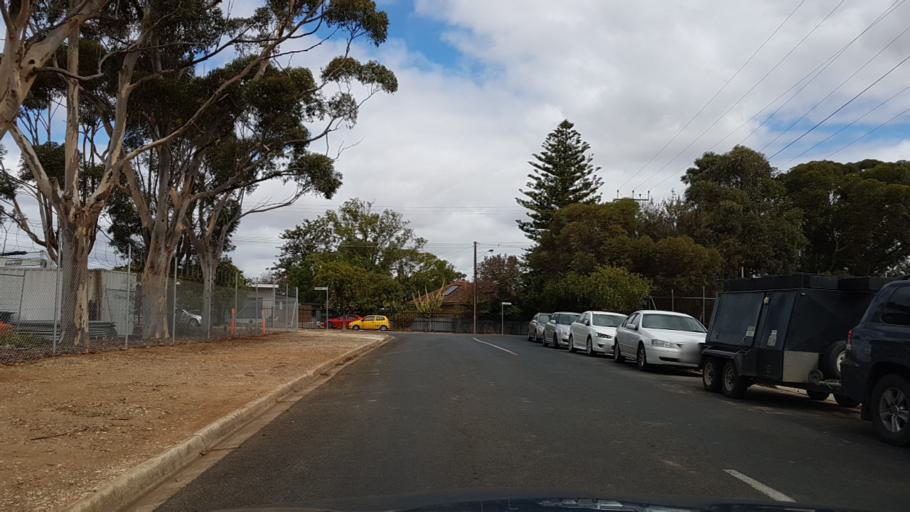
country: AU
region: South Australia
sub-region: Gawler
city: Gawler
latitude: -34.6026
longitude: 138.7603
